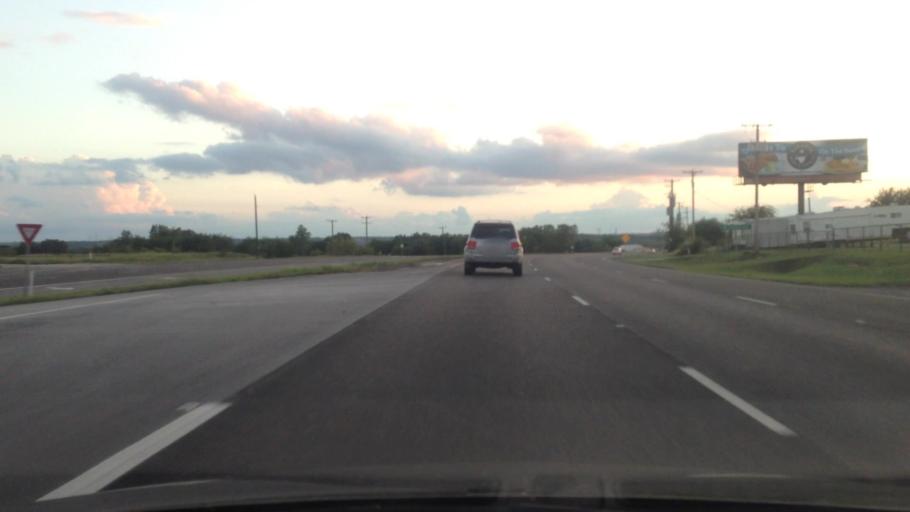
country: US
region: Texas
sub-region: Parker County
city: Aledo
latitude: 32.6050
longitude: -97.5583
